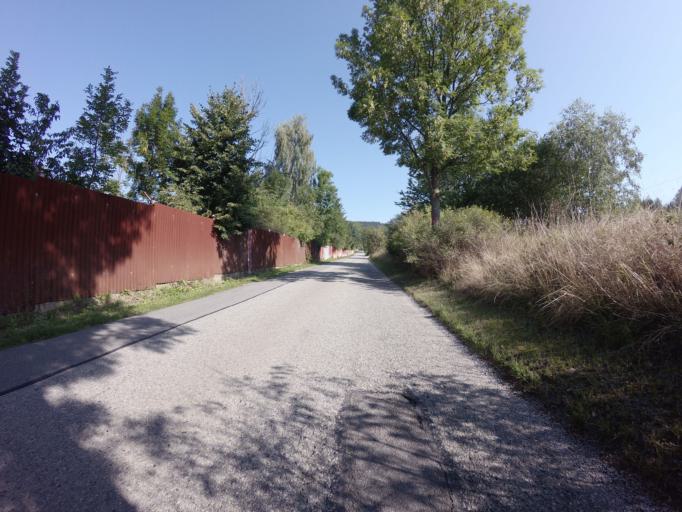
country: CZ
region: Jihocesky
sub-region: Okres Cesky Krumlov
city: Cesky Krumlov
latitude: 48.8270
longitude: 14.3113
